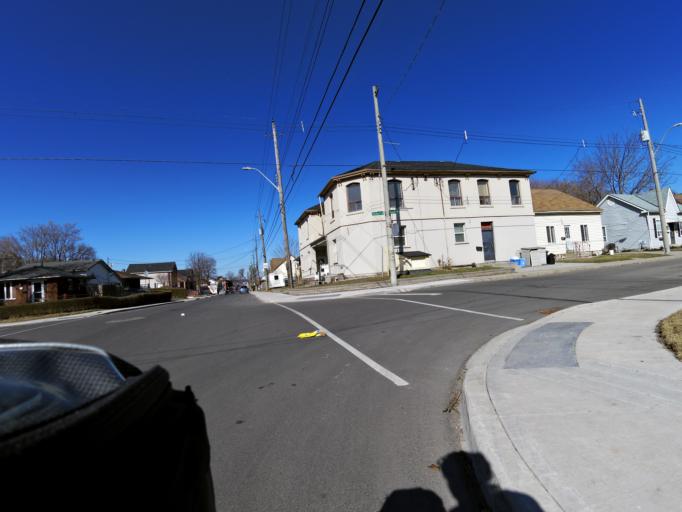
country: CA
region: Ontario
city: Hamilton
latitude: 43.2678
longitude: -79.8558
